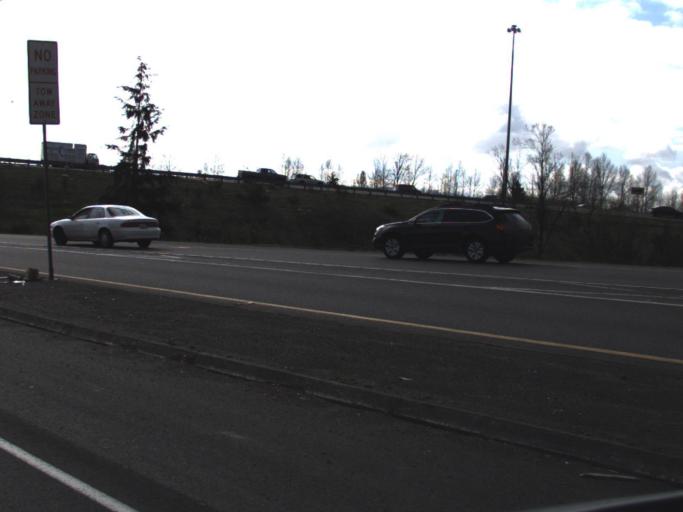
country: US
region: Washington
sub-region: King County
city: Algona
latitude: 47.3025
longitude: -122.2547
